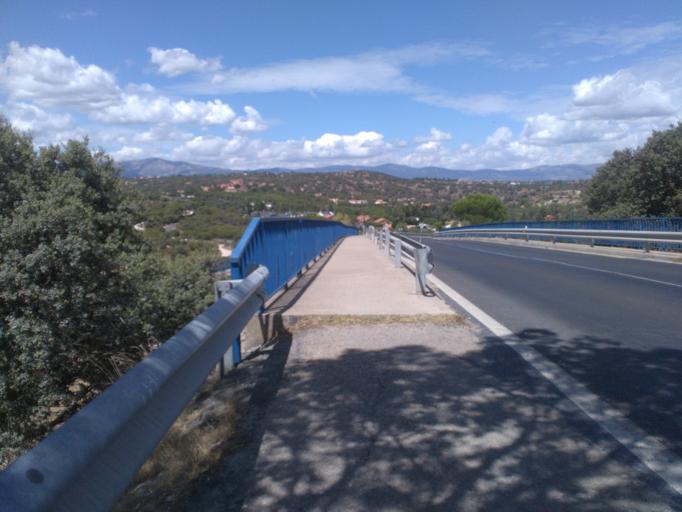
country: ES
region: Madrid
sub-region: Provincia de Madrid
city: Torrelodones
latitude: 40.5811
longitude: -3.9617
